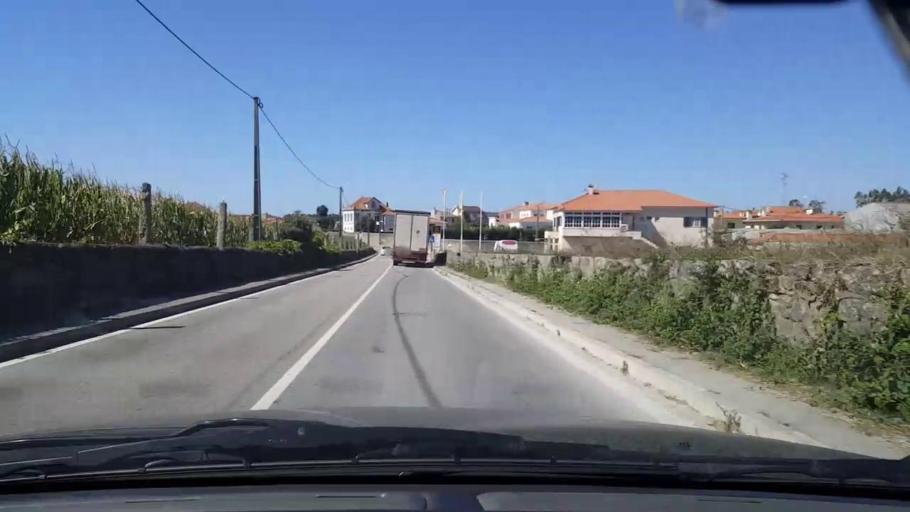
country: PT
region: Porto
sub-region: Vila do Conde
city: Arvore
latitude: 41.3407
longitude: -8.7021
